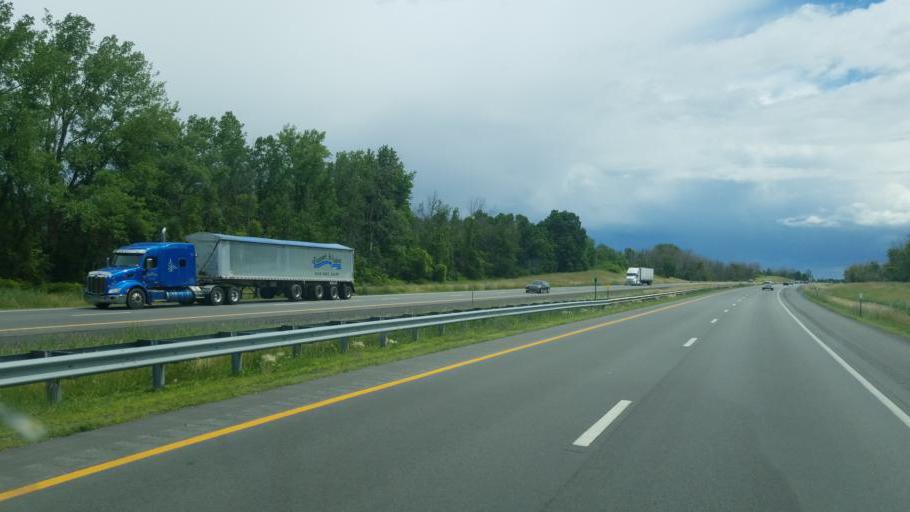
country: US
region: New York
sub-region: Monroe County
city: Scottsville
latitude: 43.0426
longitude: -77.7929
